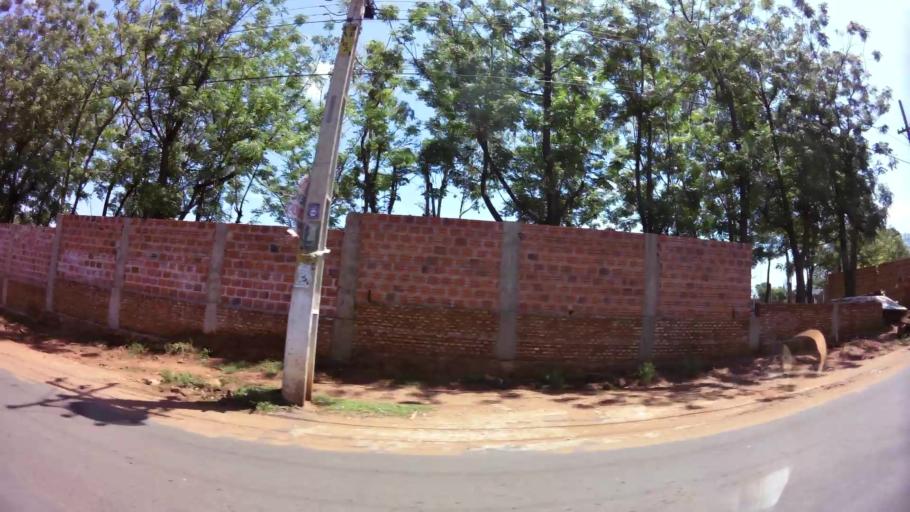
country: PY
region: Central
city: San Antonio
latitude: -25.4228
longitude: -57.5297
